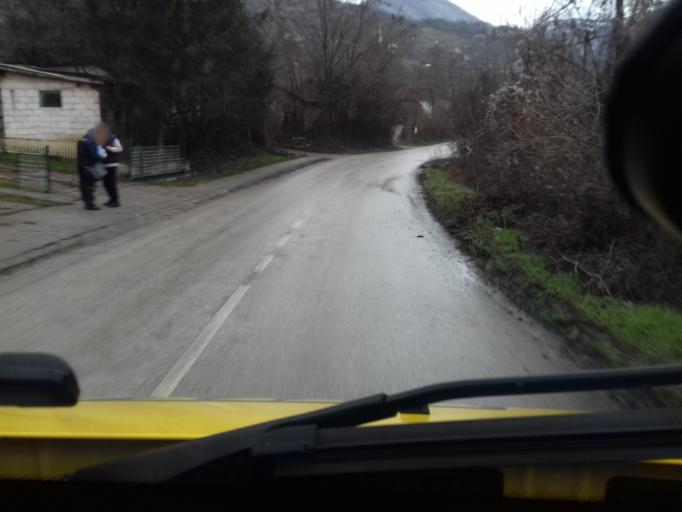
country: BA
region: Federation of Bosnia and Herzegovina
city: Zenica
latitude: 44.2350
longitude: 17.8895
